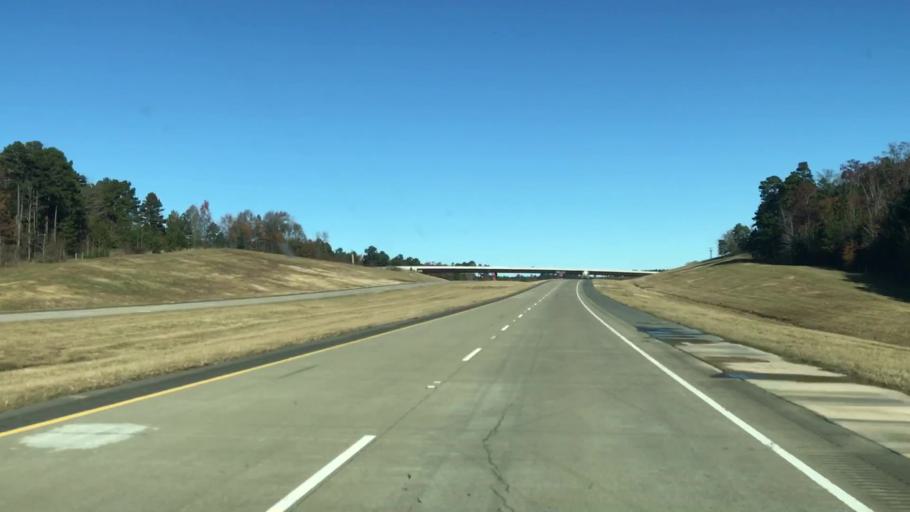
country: US
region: Louisiana
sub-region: Caddo Parish
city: Vivian
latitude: 32.9742
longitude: -93.9083
